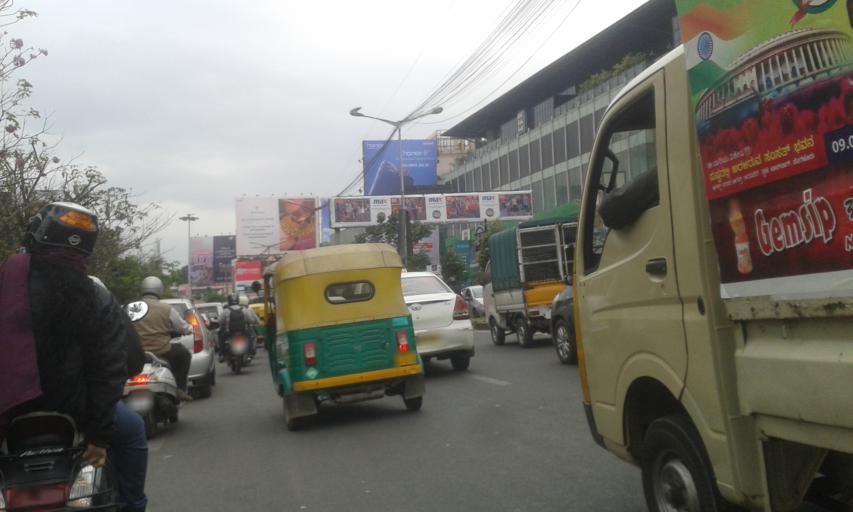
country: IN
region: Karnataka
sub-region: Bangalore Urban
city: Bangalore
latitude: 12.9341
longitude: 77.6196
